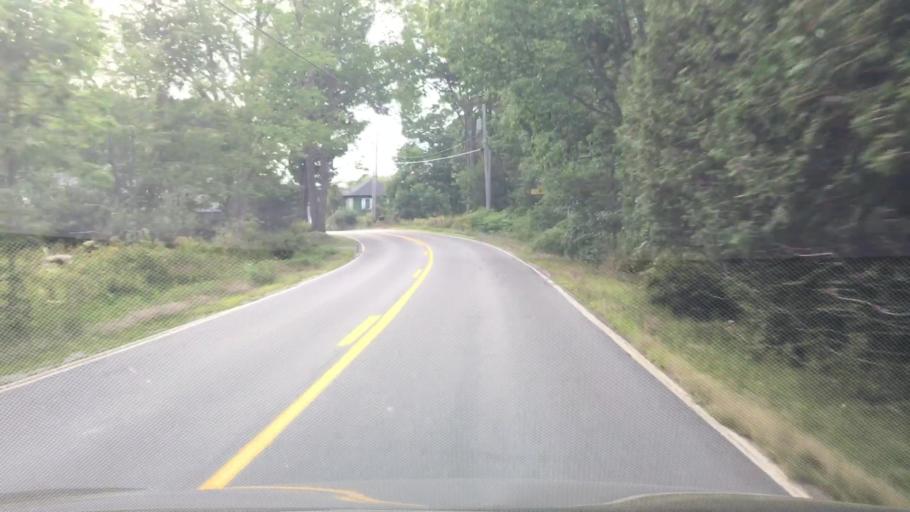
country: US
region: Maine
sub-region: Hancock County
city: Penobscot
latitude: 44.4516
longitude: -68.7000
